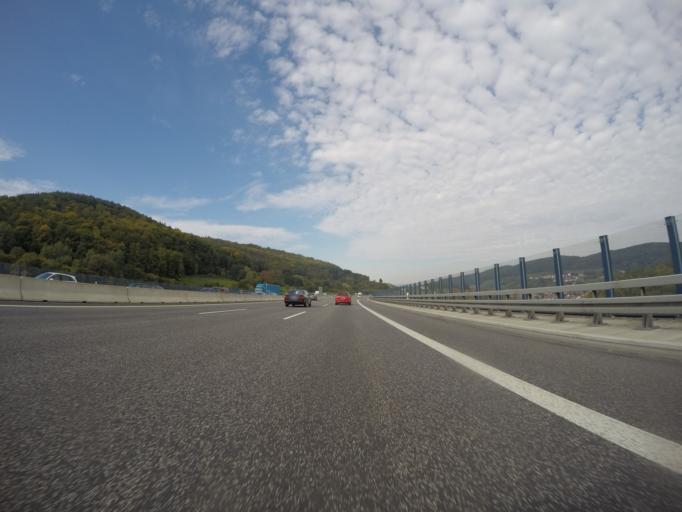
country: DE
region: Bavaria
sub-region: Regierungsbezirk Unterfranken
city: Waldaschaff
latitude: 49.9687
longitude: 9.2975
